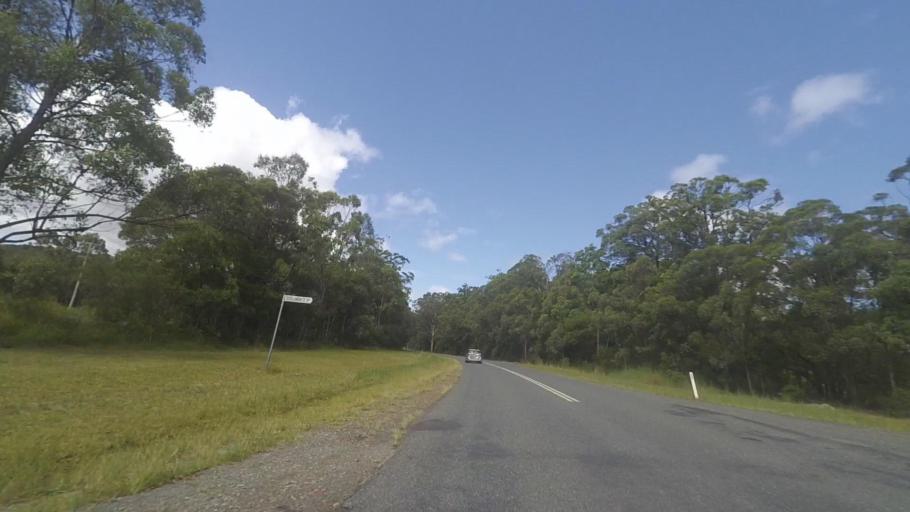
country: AU
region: New South Wales
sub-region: Great Lakes
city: Bulahdelah
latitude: -32.4035
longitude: 152.2787
